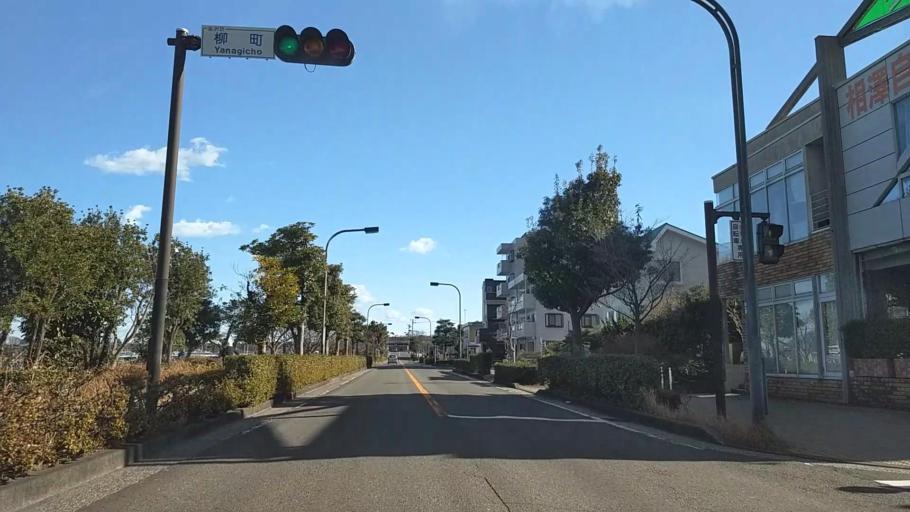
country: JP
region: Kanagawa
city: Yokosuka
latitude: 35.3277
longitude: 139.6267
